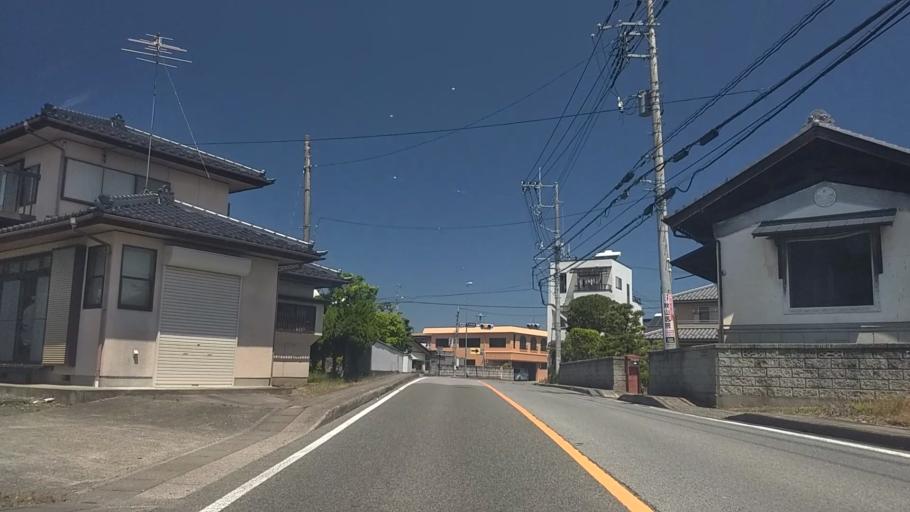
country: JP
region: Yamanashi
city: Nirasaki
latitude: 35.6814
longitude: 138.4636
